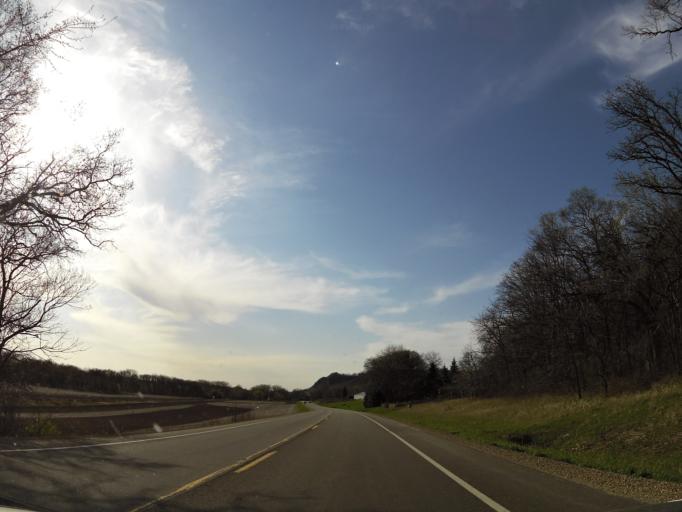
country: US
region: Minnesota
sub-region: Goodhue County
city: Red Wing
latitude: 44.6416
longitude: -92.6019
